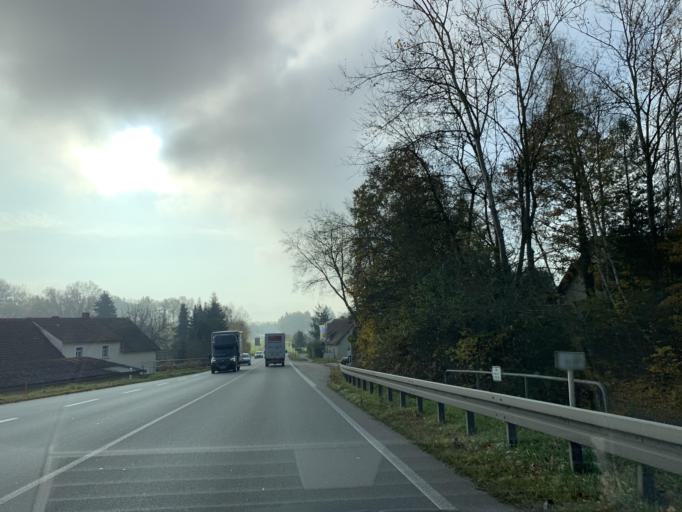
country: DE
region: Bavaria
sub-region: Upper Palatinate
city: Bruck in der Oberpfalz
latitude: 49.2641
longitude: 12.2953
